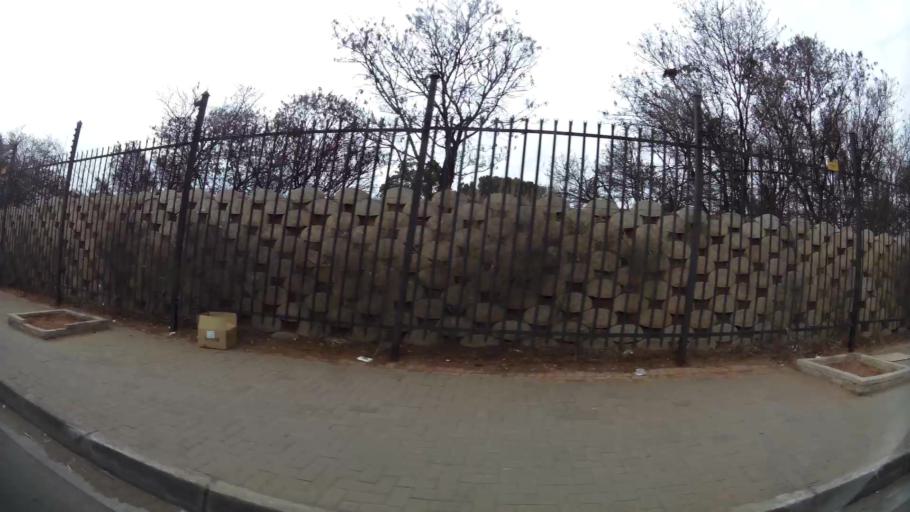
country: ZA
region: Orange Free State
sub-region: Mangaung Metropolitan Municipality
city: Bloemfontein
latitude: -29.1132
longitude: 26.2016
